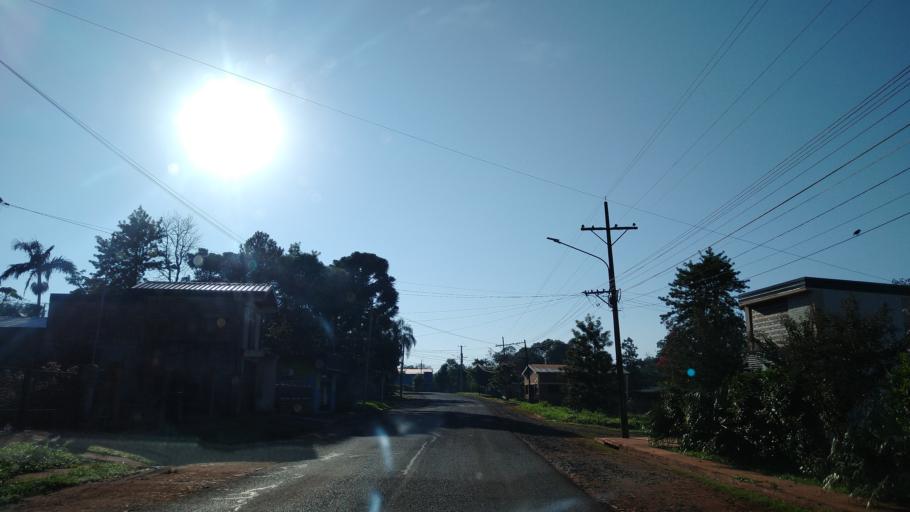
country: AR
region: Misiones
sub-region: Departamento de Montecarlo
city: Montecarlo
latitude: -26.5698
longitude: -54.7607
